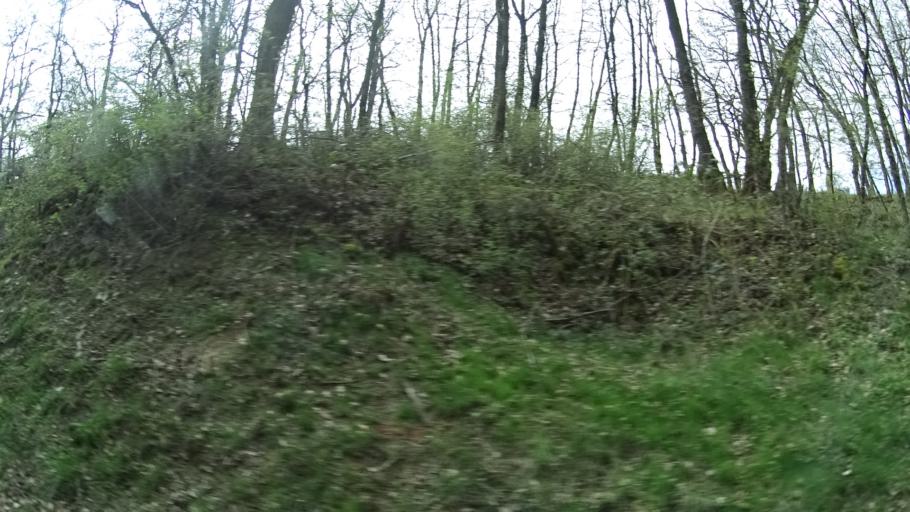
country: DE
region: Rheinland-Pfalz
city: Weitersbach
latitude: 49.8731
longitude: 7.3259
